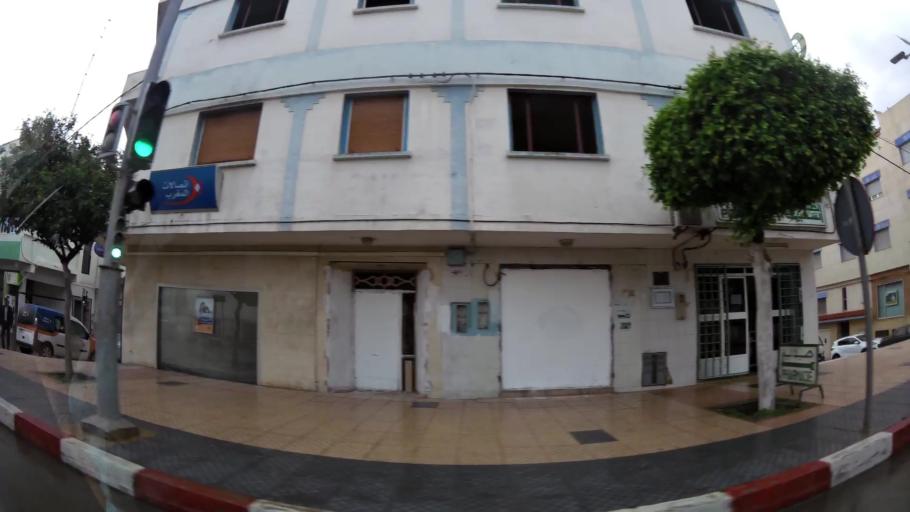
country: MA
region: Oriental
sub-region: Nador
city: Nador
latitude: 35.1549
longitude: -2.9997
